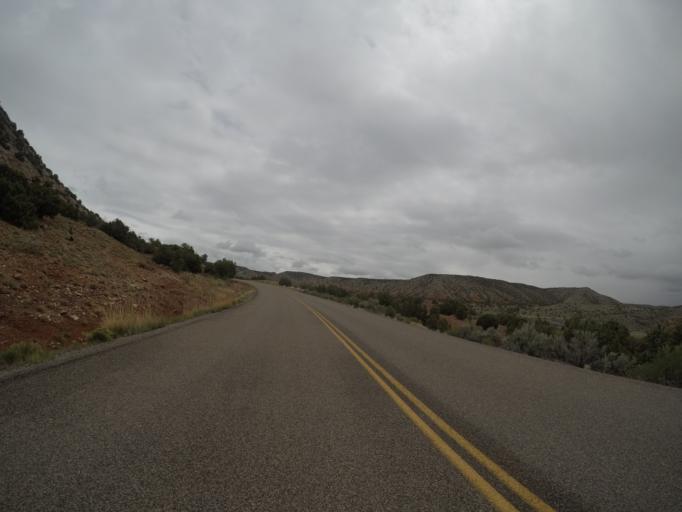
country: US
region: Wyoming
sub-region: Big Horn County
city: Lovell
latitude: 45.0975
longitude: -108.2153
